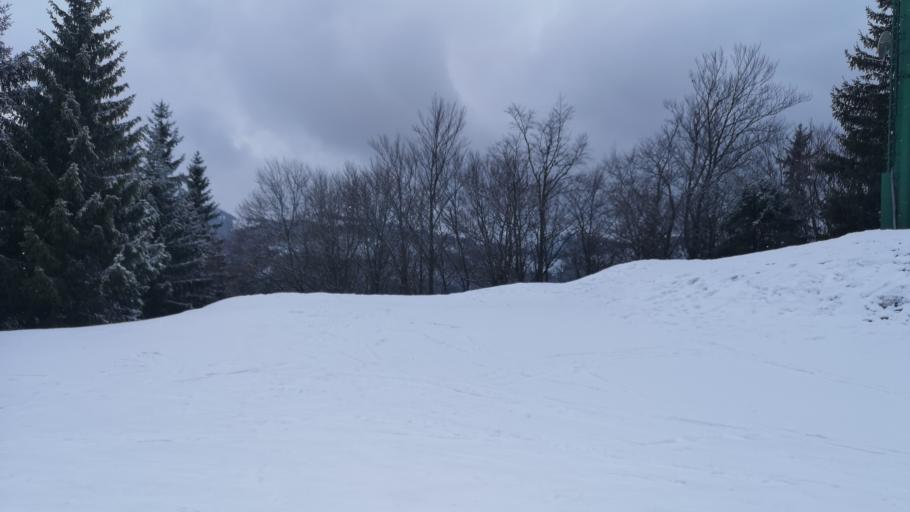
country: SK
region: Zilinsky
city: Ruzomberok
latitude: 49.0489
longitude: 19.2489
